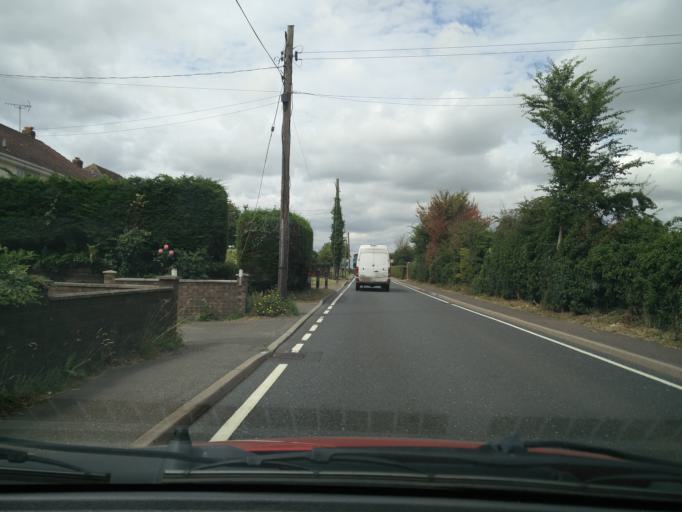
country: GB
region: England
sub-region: Essex
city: Burnham on Crouch
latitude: 51.6555
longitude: 0.7609
